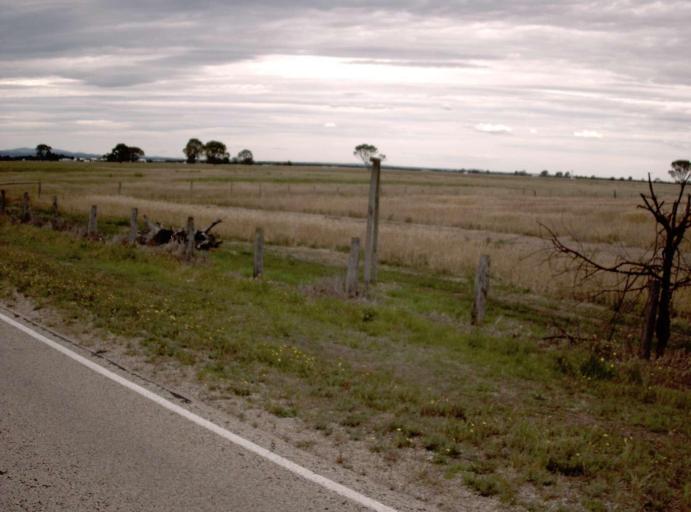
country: AU
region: Victoria
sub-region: East Gippsland
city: Bairnsdale
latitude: -37.8926
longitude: 147.5561
